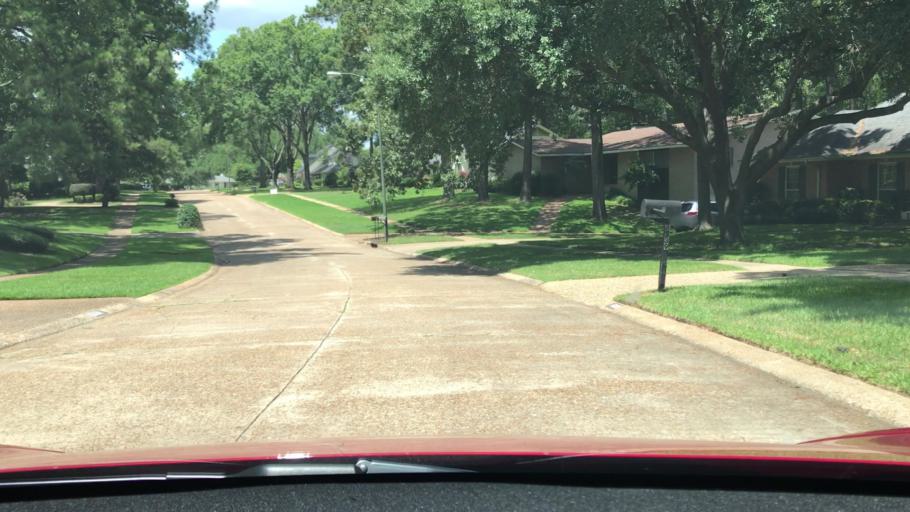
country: US
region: Louisiana
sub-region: Bossier Parish
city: Bossier City
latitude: 32.4308
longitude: -93.7339
